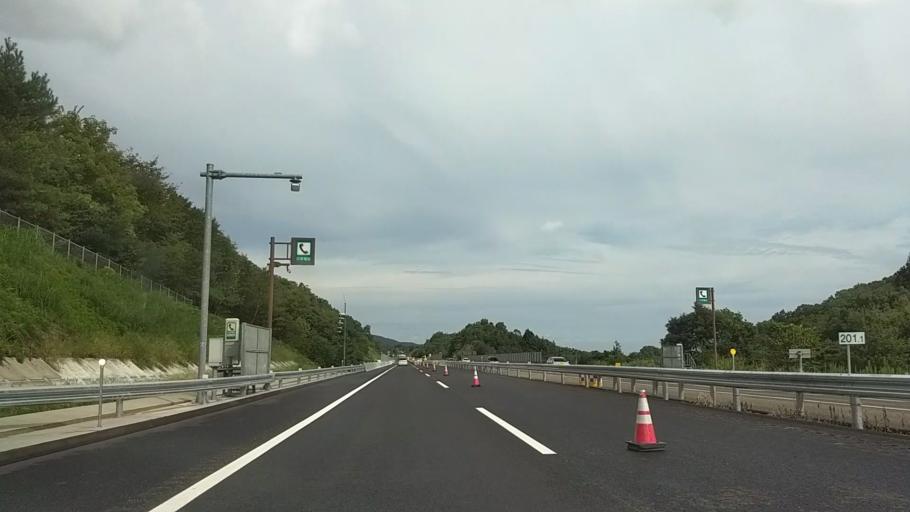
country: JP
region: Niigata
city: Joetsu
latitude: 37.1079
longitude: 138.2192
